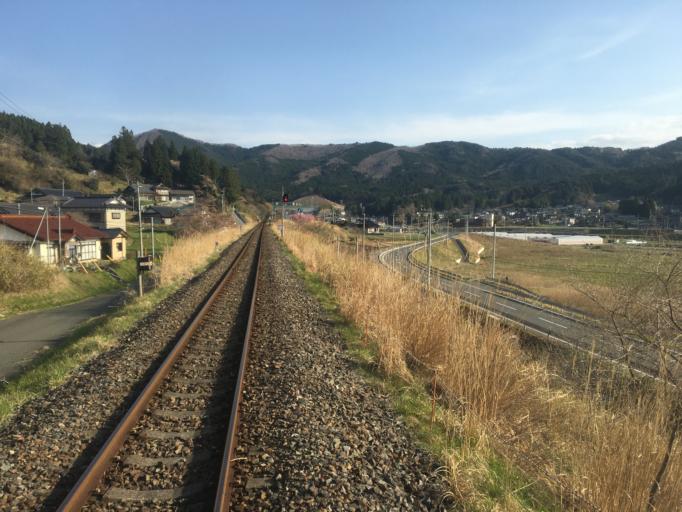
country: JP
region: Iwate
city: Ofunato
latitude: 39.1139
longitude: 141.8101
